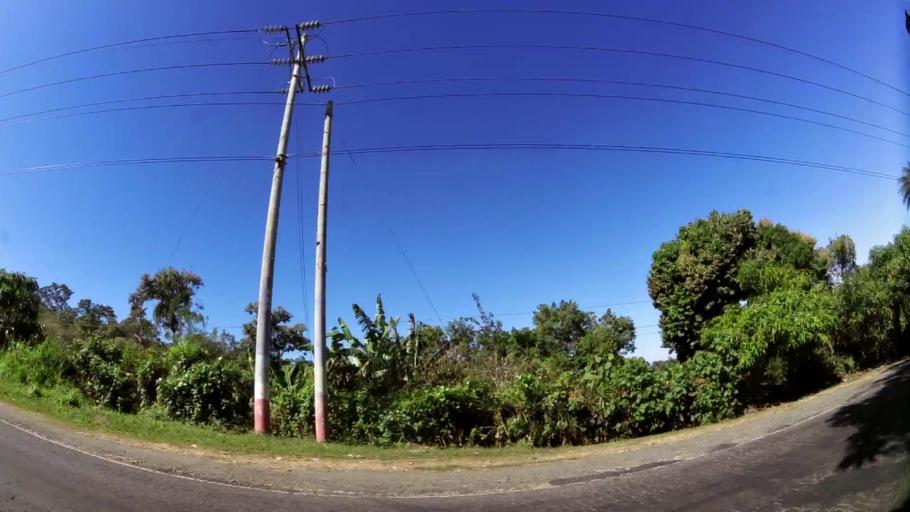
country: SV
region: Ahuachapan
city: Ahuachapan
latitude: 13.9045
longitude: -89.8336
